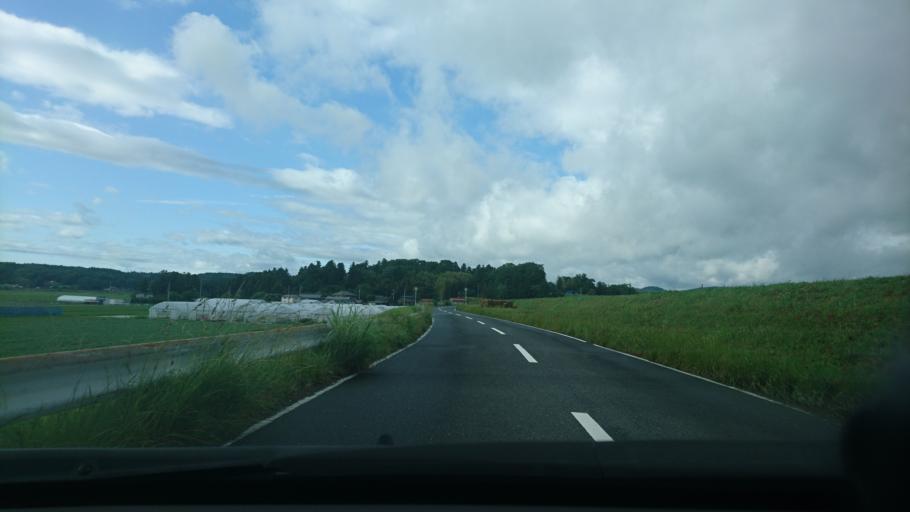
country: JP
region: Miyagi
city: Wakuya
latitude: 38.6866
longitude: 141.2836
